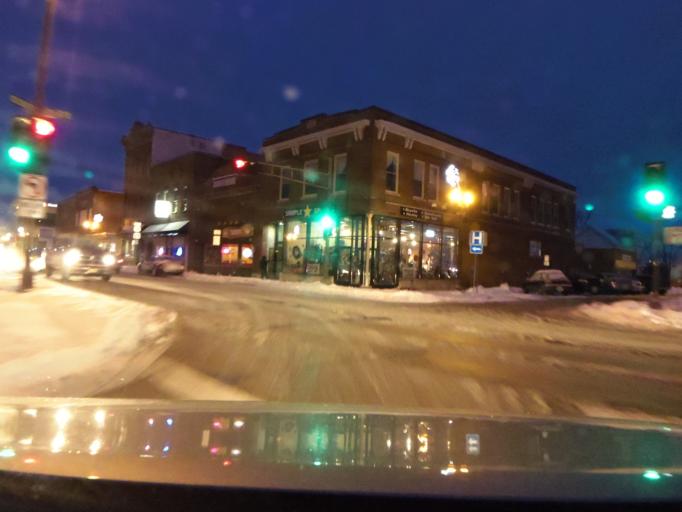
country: US
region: Wisconsin
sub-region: Dunn County
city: Menomonie
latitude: 44.8766
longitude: -91.9260
